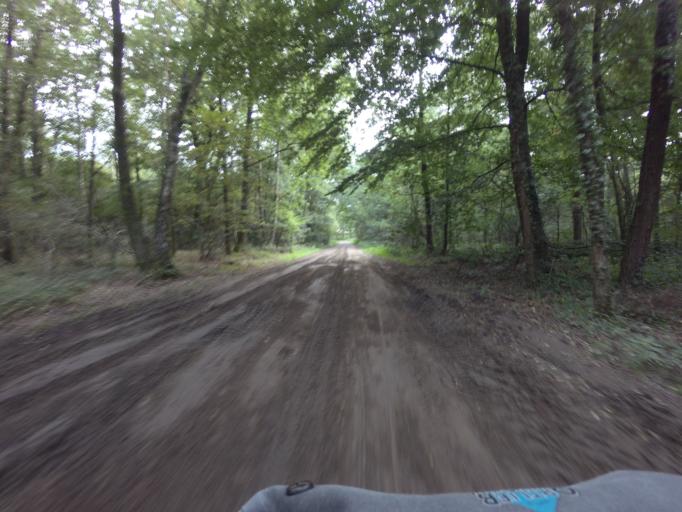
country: DE
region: Lower Saxony
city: Getelo
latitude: 52.4512
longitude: 6.8482
